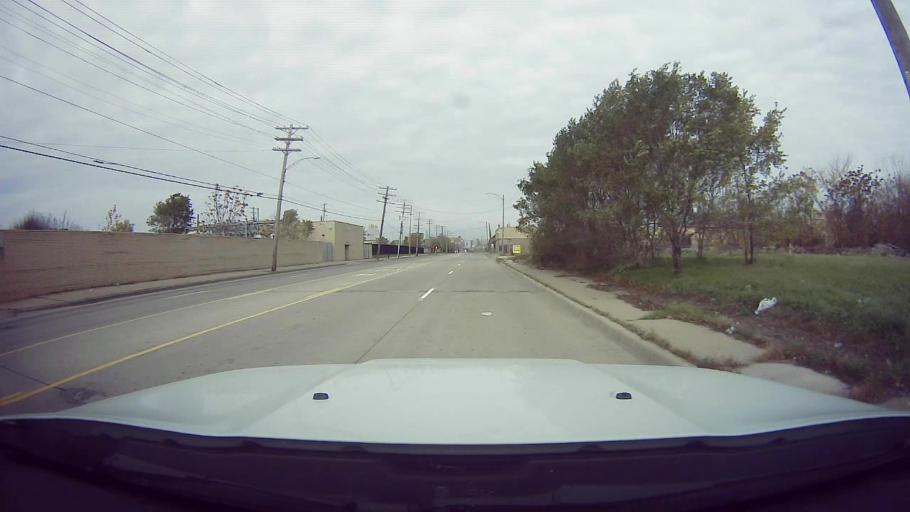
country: US
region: Michigan
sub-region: Wayne County
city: Hamtramck
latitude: 42.3647
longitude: -83.0525
